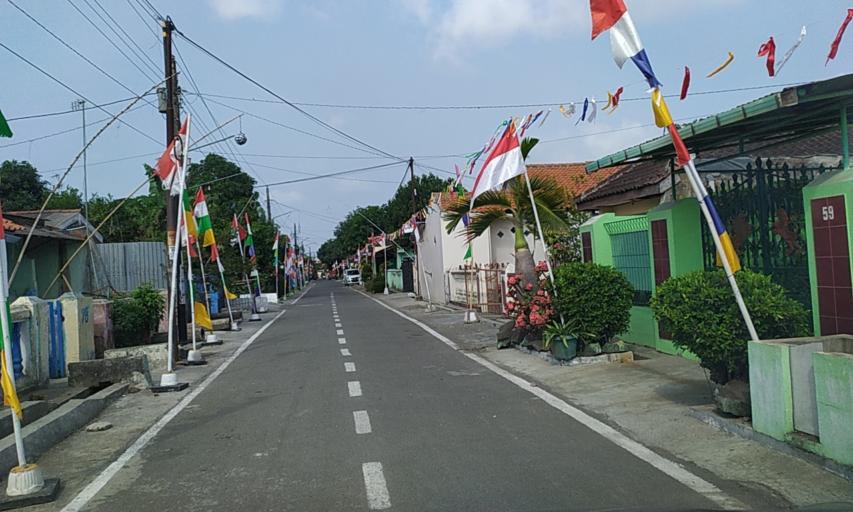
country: ID
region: Central Java
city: Karangbadar Kidul
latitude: -7.7301
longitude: 108.9990
